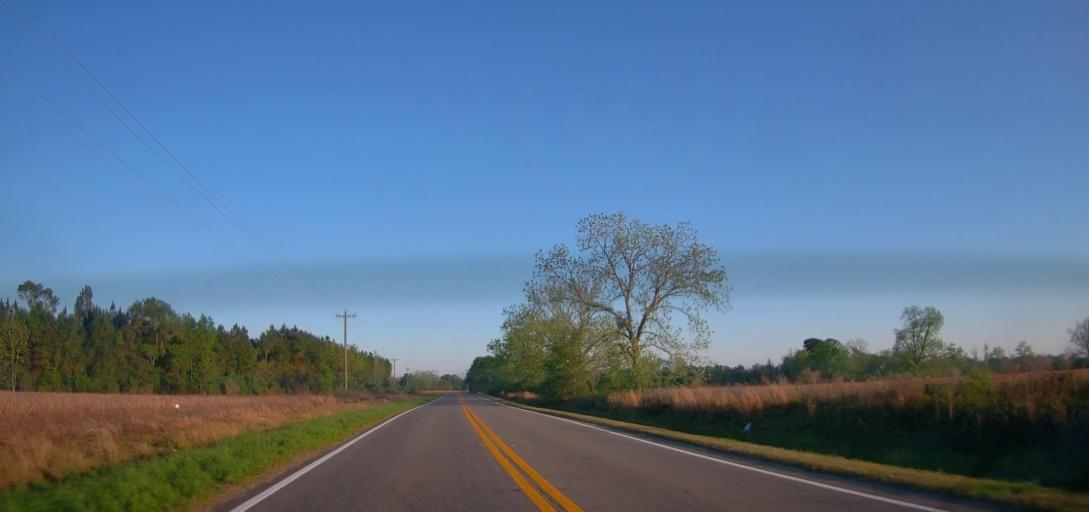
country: US
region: Georgia
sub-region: Irwin County
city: Ocilla
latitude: 31.6154
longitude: -83.2652
